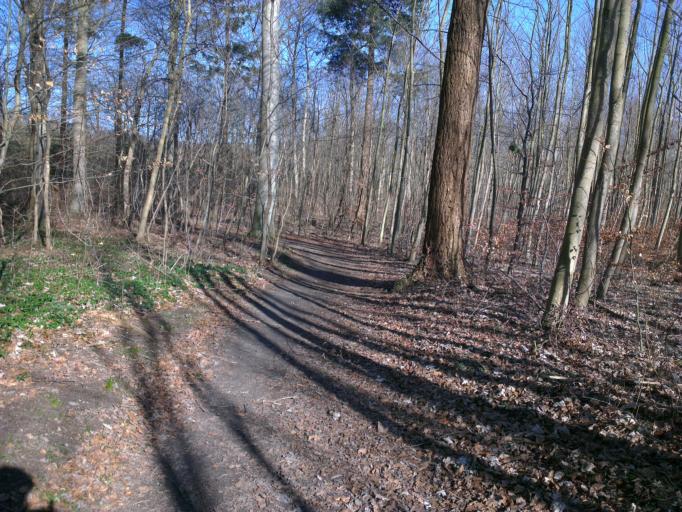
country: DK
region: Capital Region
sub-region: Frederikssund Kommune
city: Jaegerspris
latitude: 55.8649
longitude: 11.9788
